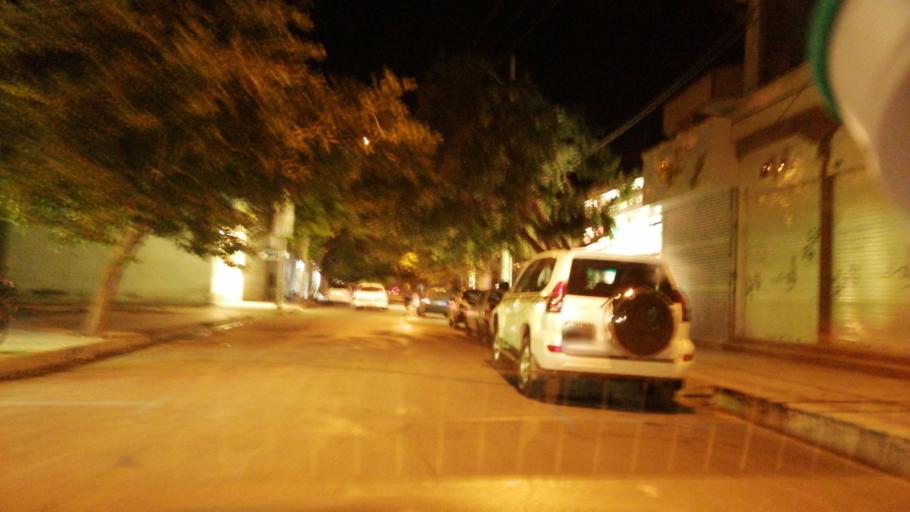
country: IR
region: Razavi Khorasan
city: Mashhad
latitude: 36.3076
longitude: 59.6007
